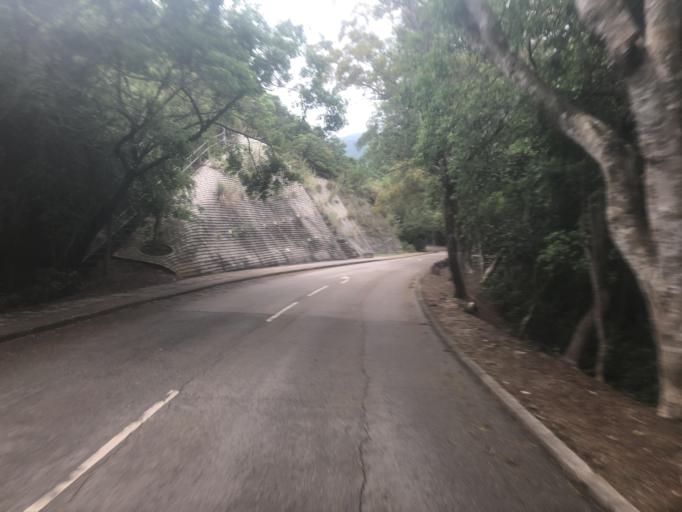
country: HK
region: Sai Kung
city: Sai Kung
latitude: 22.3980
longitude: 114.3258
